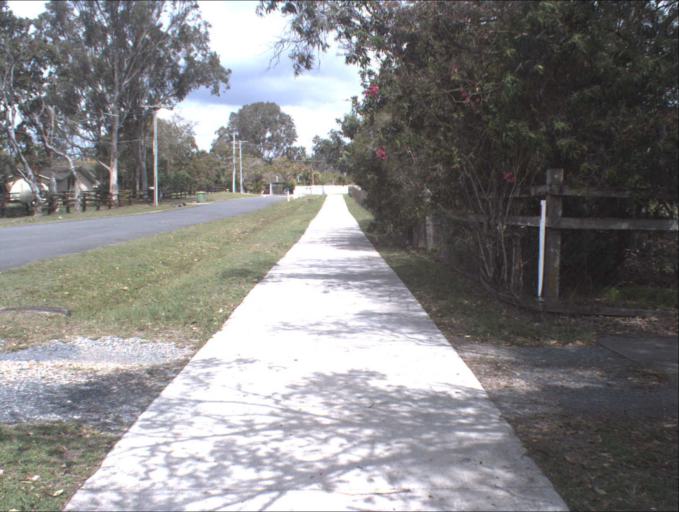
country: AU
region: Queensland
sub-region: Logan
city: Waterford West
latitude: -27.6977
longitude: 153.1329
